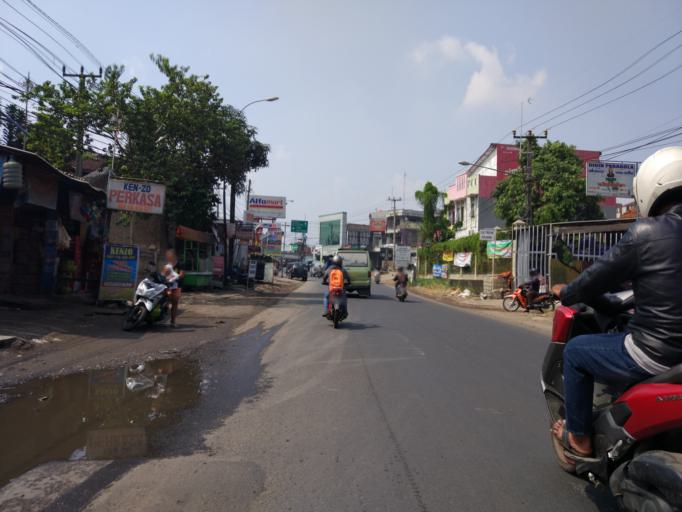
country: ID
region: West Java
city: Cileunyi
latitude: -6.9396
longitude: 107.7493
